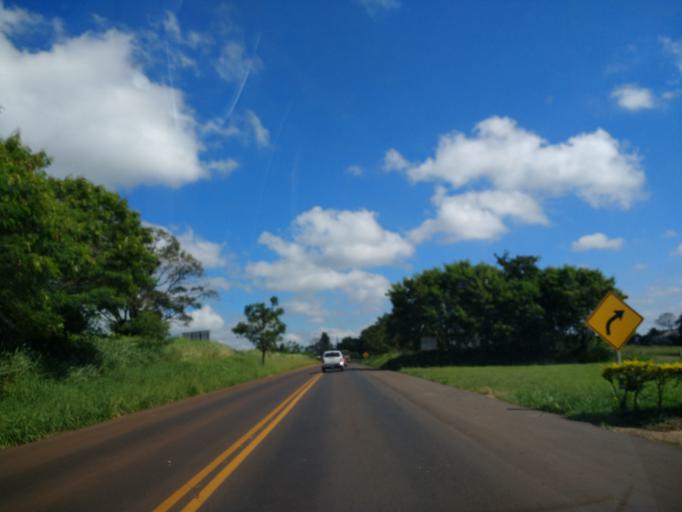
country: BR
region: Parana
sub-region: Umuarama
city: Umuarama
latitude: -23.8224
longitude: -53.3369
